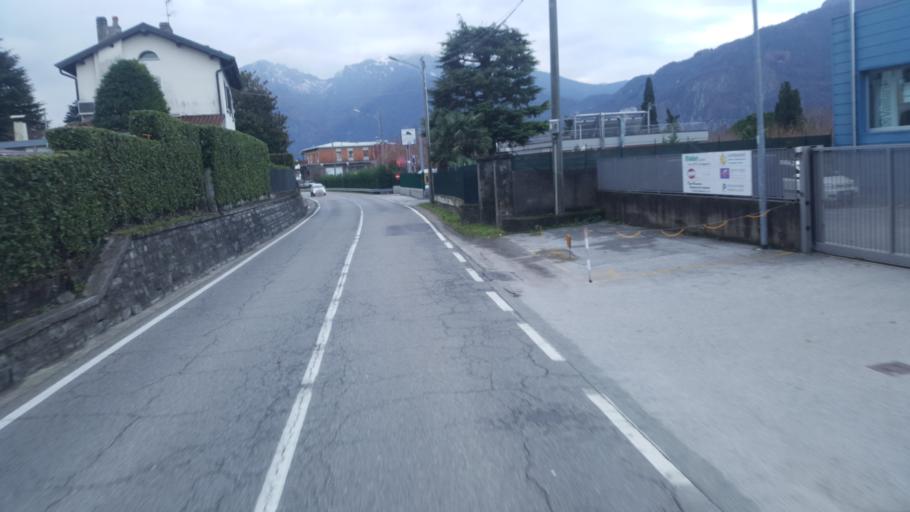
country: IT
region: Lombardy
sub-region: Provincia di Lecco
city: Mandello del Lario
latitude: 45.9222
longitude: 9.3129
